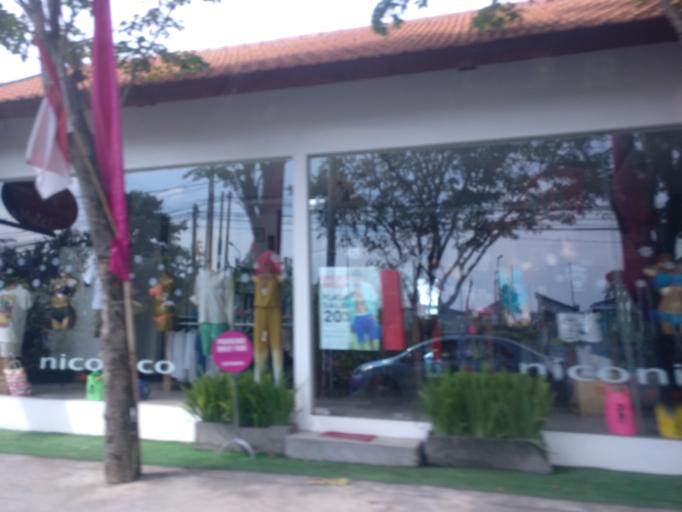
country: ID
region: Bali
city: Banjar Gunungpande
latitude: -8.6608
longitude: 115.1448
